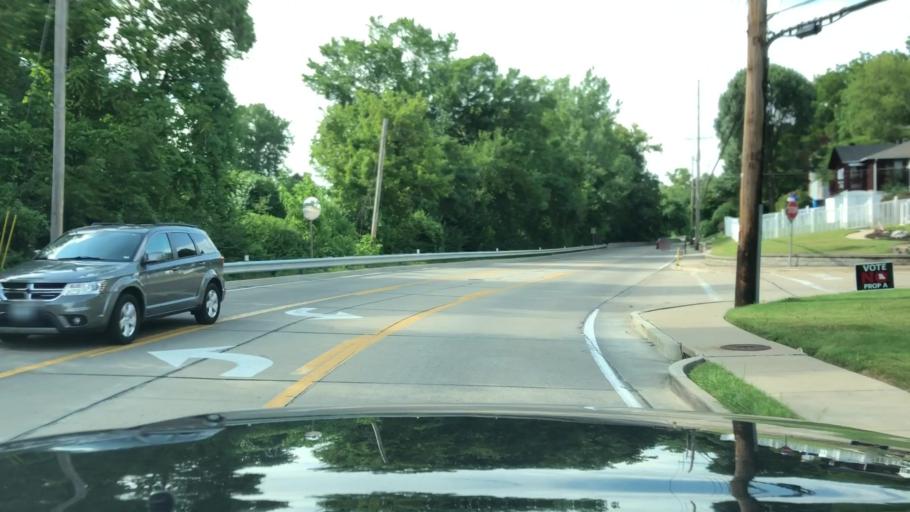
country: US
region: Missouri
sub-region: Saint Charles County
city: Saint Charles
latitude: 38.8100
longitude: -90.5128
